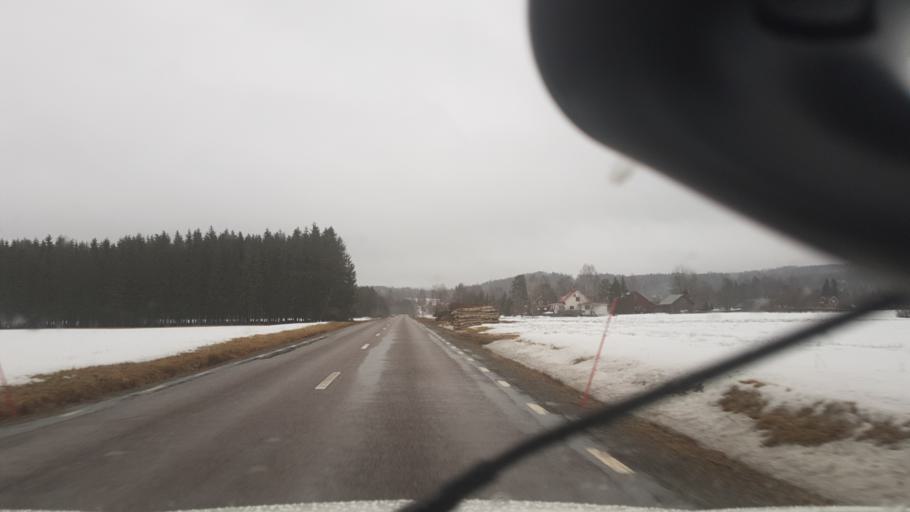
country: SE
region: Vaermland
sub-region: Arjangs Kommun
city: Arjaeng
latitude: 59.5944
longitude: 12.1392
